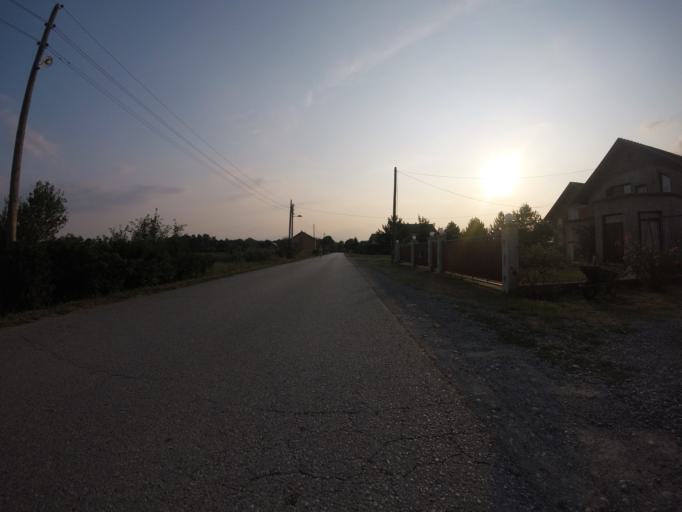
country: HR
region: Zagrebacka
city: Micevec
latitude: 45.7515
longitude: 16.1238
